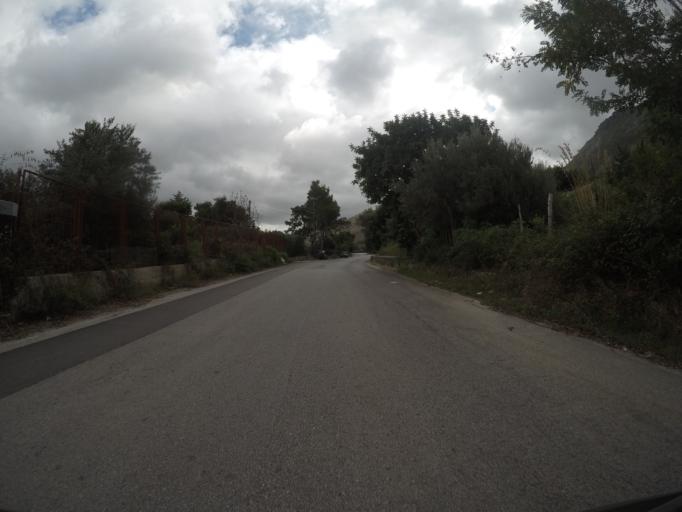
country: IT
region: Sicily
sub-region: Palermo
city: Montelepre
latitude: 38.1207
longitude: 13.1845
